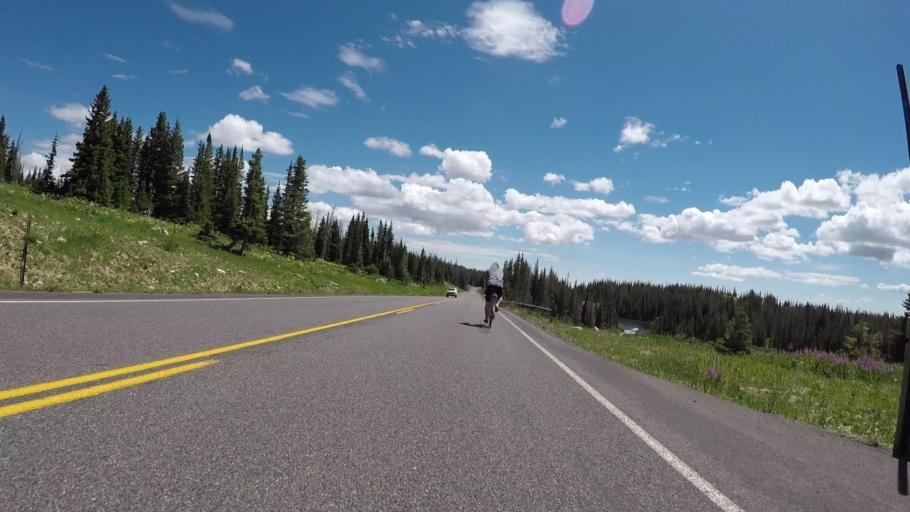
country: US
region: Wyoming
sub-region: Carbon County
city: Saratoga
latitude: 41.3513
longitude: -106.2726
